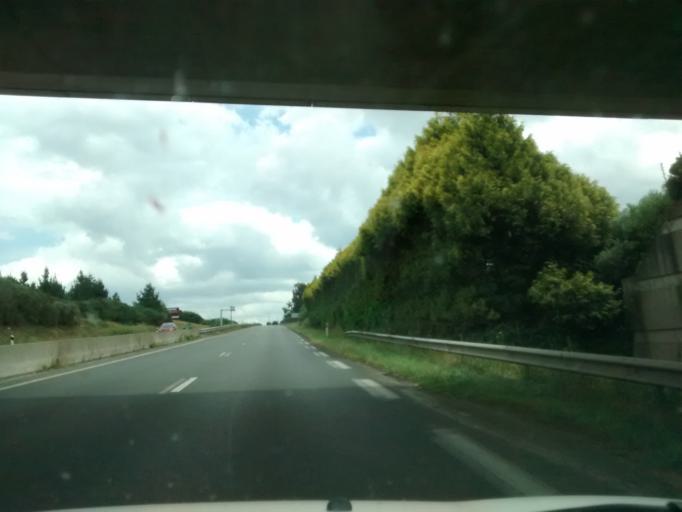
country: FR
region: Brittany
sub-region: Departement des Cotes-d'Armor
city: Rospez
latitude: 48.7183
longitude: -3.4134
